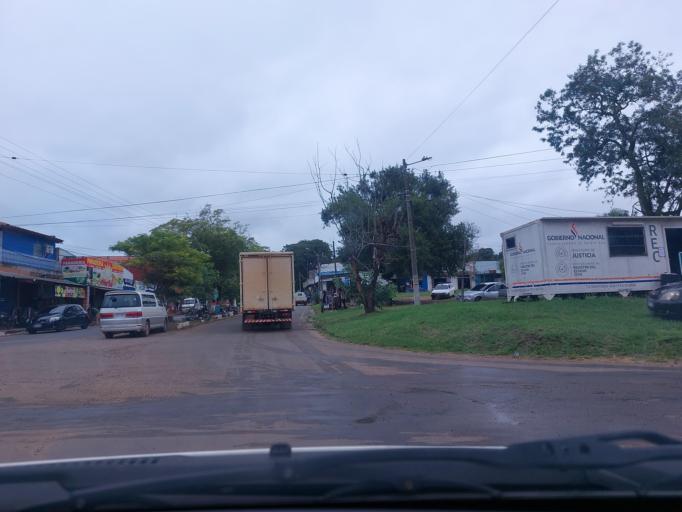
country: PY
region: San Pedro
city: Guayaybi
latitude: -24.6655
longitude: -56.4390
